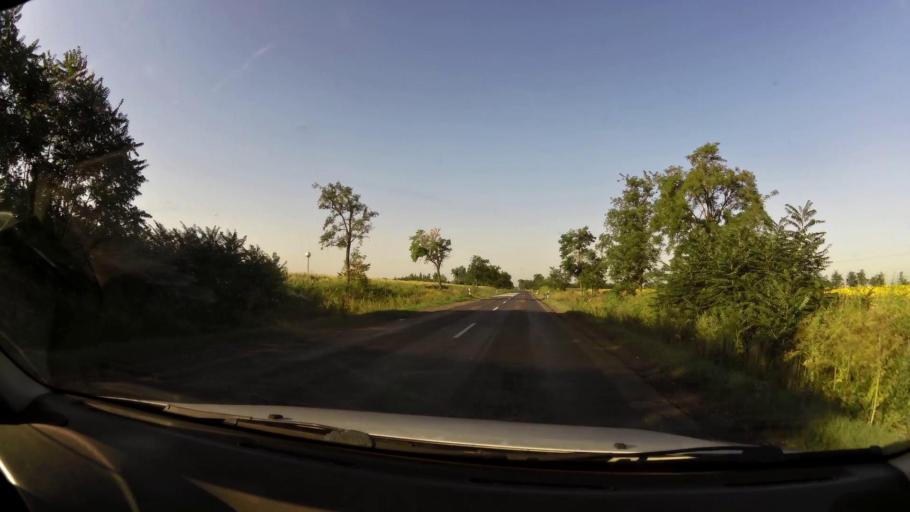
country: HU
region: Pest
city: Cegled
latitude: 47.2316
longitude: 19.8360
